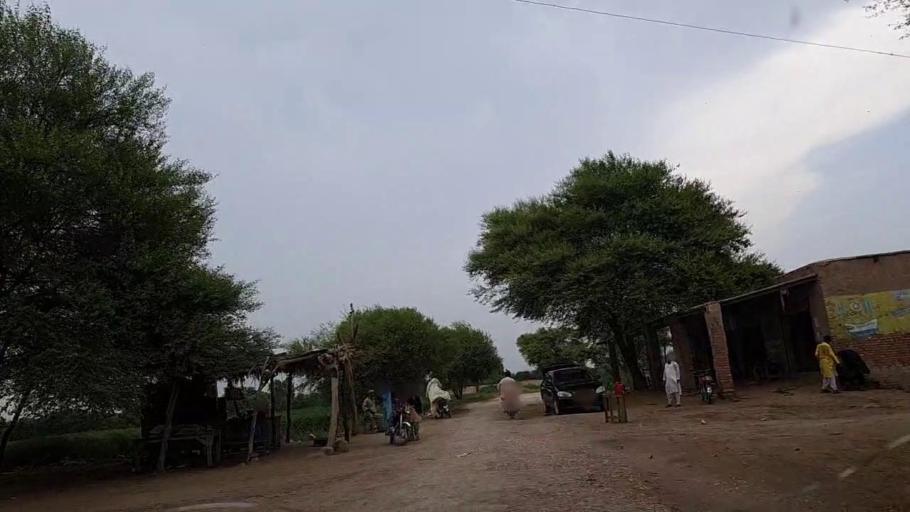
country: PK
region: Sindh
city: Mirpur Mathelo
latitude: 27.8403
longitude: 69.6197
